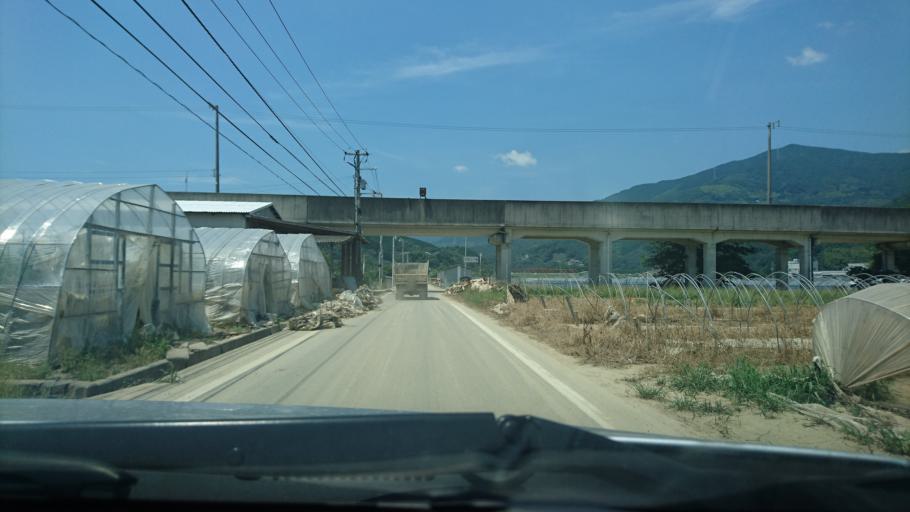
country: JP
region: Ehime
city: Ozu
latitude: 33.5328
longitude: 132.5677
